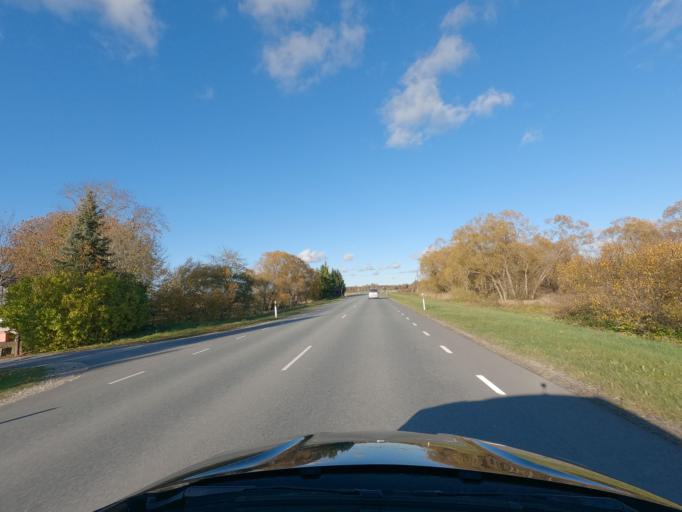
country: EE
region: Saare
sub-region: Kuressaare linn
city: Kuressaare
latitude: 58.3002
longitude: 22.5766
